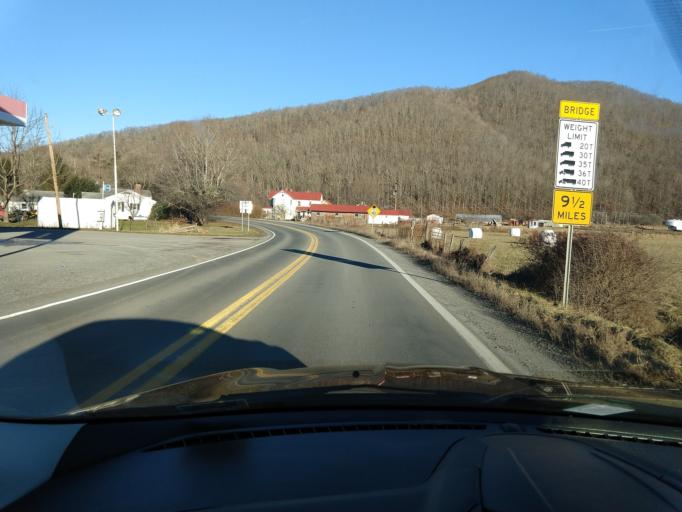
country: US
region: Virginia
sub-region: Highland County
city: Monterey
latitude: 38.5412
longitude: -79.7830
